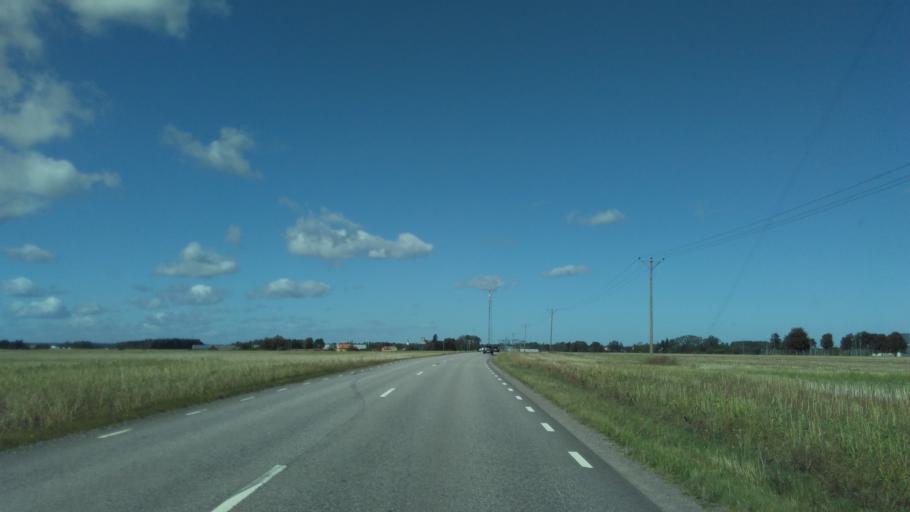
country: SE
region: Vaestra Goetaland
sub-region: Vara Kommun
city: Vara
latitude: 58.2387
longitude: 12.9965
